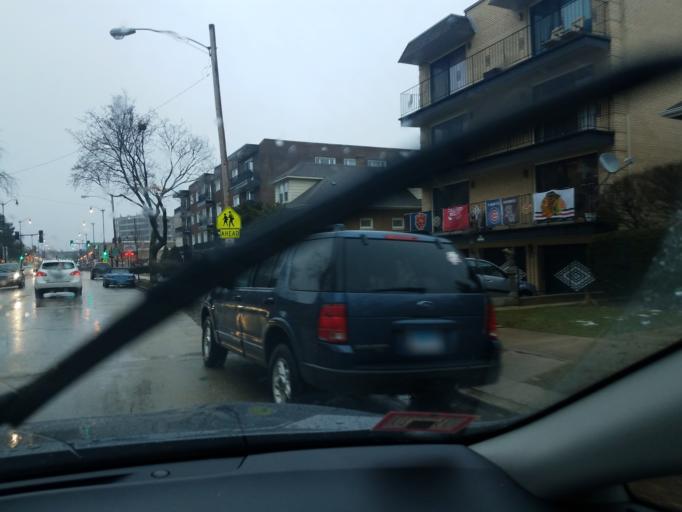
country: US
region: Illinois
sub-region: Cook County
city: Skokie
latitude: 42.0239
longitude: -87.7567
